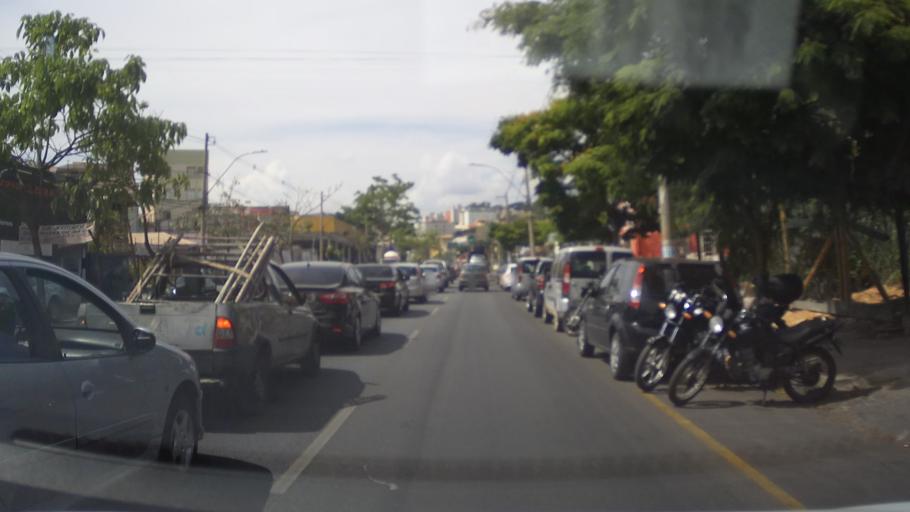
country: BR
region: Minas Gerais
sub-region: Belo Horizonte
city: Belo Horizonte
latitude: -19.9466
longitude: -43.9695
